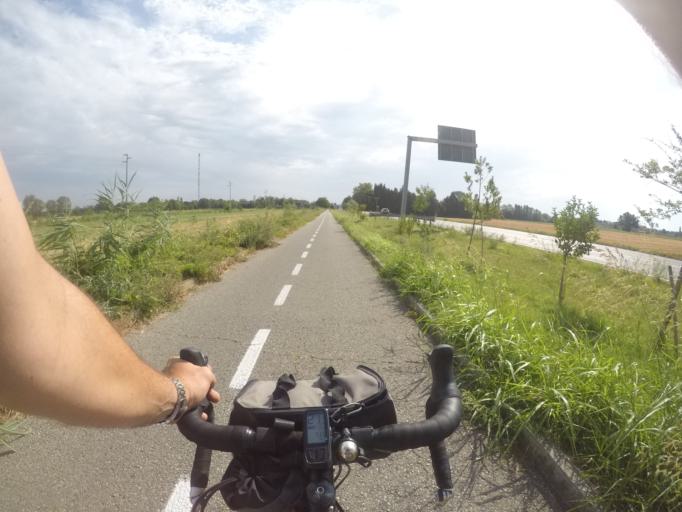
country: IT
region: Emilia-Romagna
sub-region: Provincia di Ravenna
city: Porto Fuori
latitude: 44.4194
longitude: 12.2325
